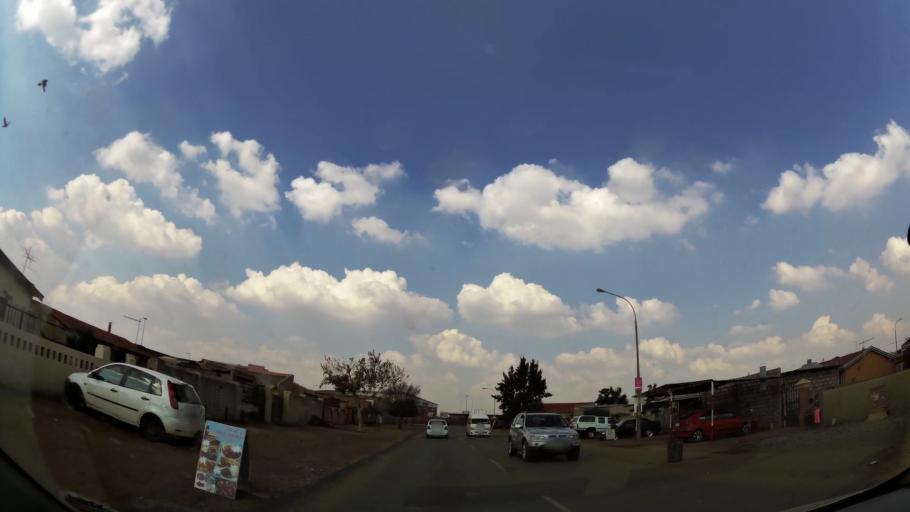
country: ZA
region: Gauteng
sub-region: Ekurhuleni Metropolitan Municipality
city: Germiston
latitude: -26.3468
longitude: 28.1393
